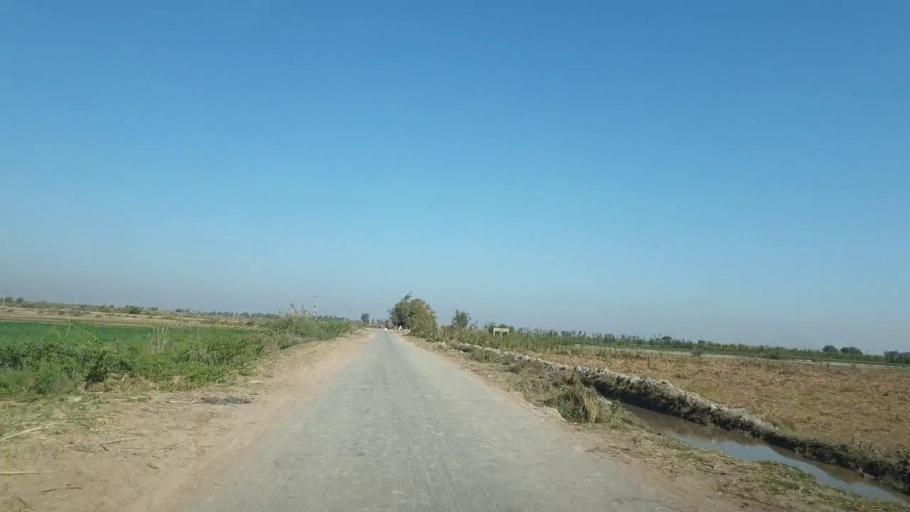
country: PK
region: Sindh
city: Mirpur Khas
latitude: 25.6020
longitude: 69.0450
